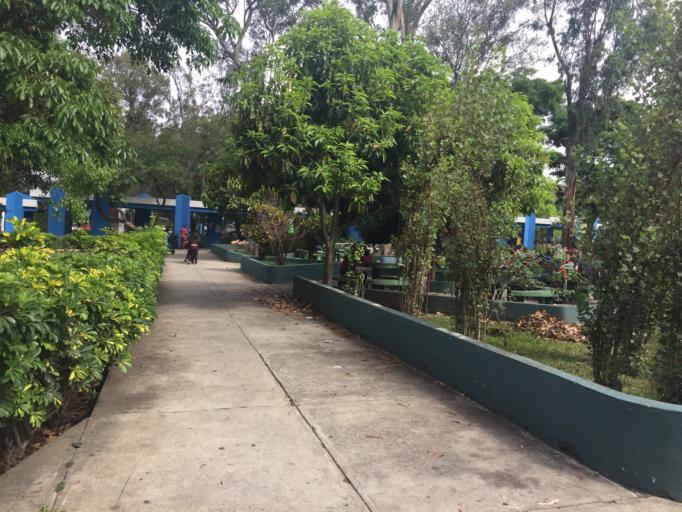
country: GT
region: Guatemala
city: Santa Catarina Pinula
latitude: 14.5865
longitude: -90.5522
